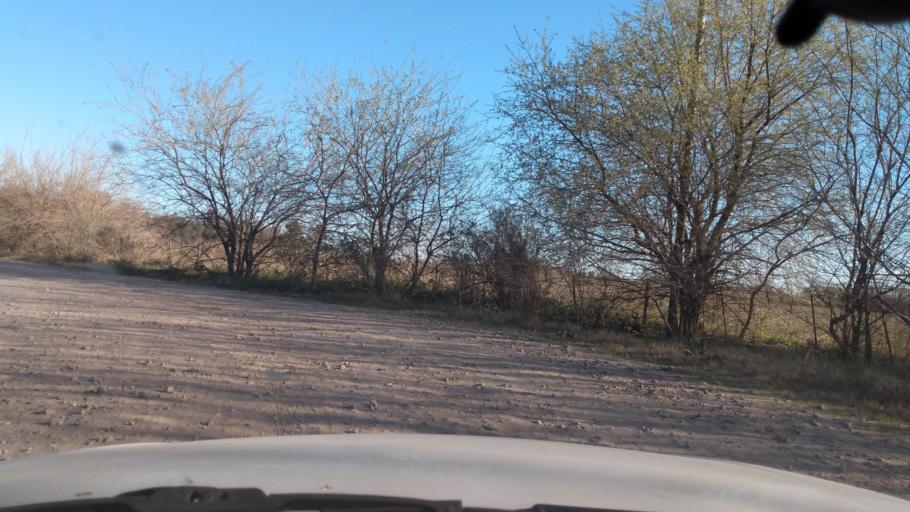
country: AR
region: Buenos Aires
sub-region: Partido de Mercedes
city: Mercedes
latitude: -34.6032
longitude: -59.2911
